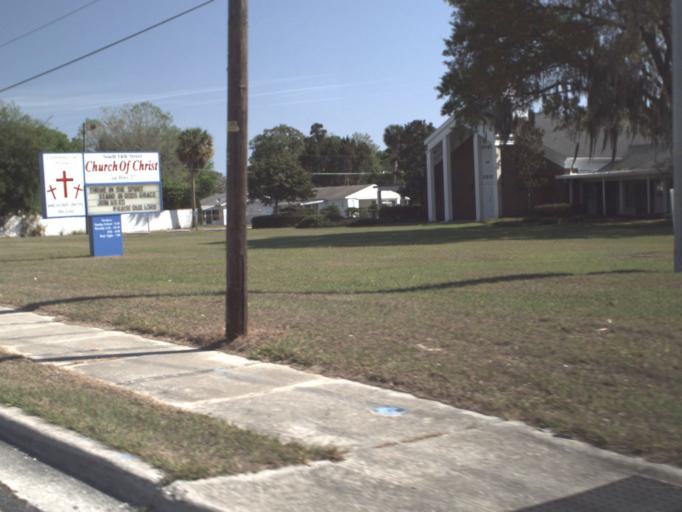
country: US
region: Florida
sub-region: Lake County
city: Leesburg
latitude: 28.7950
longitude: -81.8876
